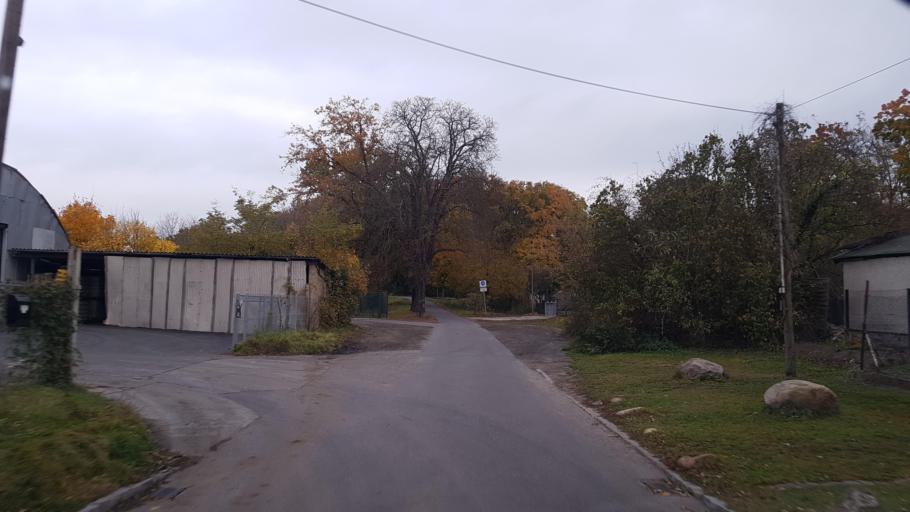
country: DE
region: Brandenburg
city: Spremberg
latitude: 51.5763
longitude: 14.3692
